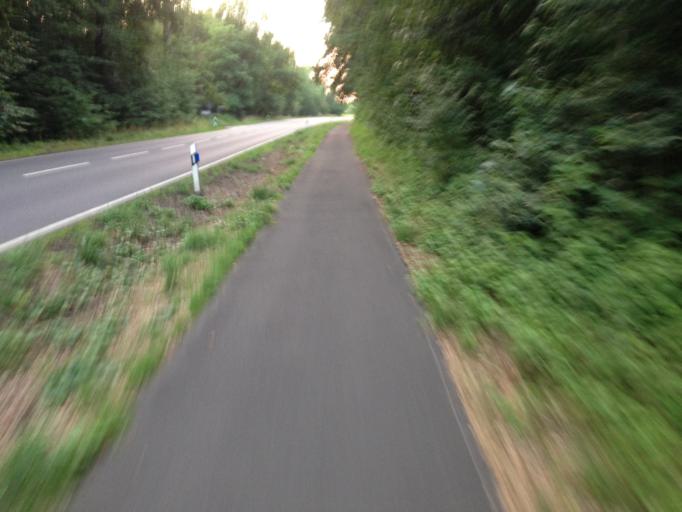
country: DE
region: Hesse
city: Allendorf an der Lahn
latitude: 50.5490
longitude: 8.6475
